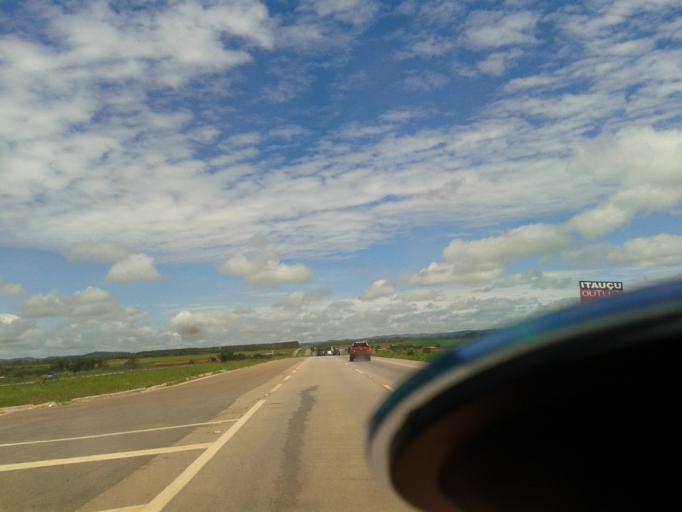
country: BR
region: Goias
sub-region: Inhumas
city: Inhumas
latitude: -16.3068
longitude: -49.5277
